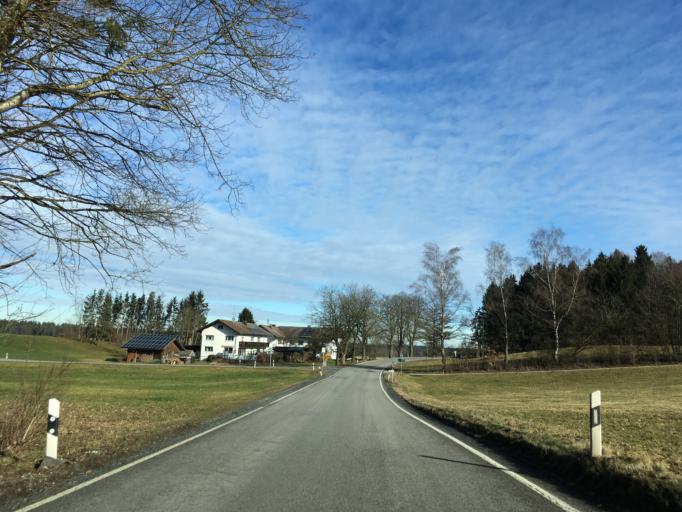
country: DE
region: Bavaria
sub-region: Upper Bavaria
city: Unterreit
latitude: 48.1099
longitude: 12.3128
